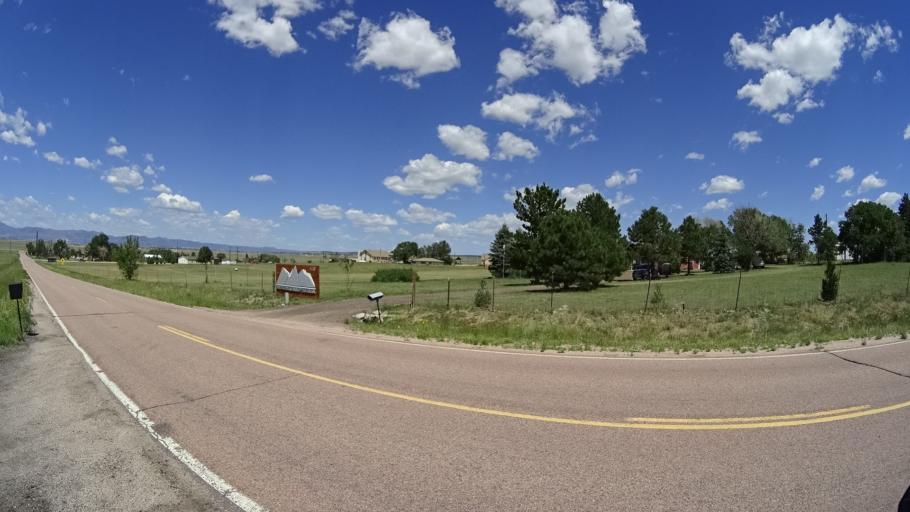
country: US
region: Colorado
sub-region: El Paso County
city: Cimarron Hills
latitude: 38.9116
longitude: -104.6193
